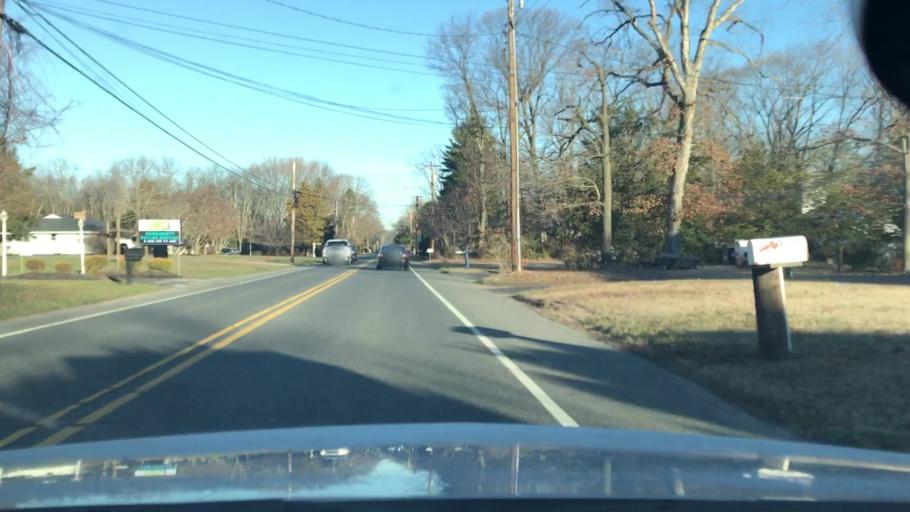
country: US
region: New Jersey
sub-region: Gloucester County
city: Williamstown
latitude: 39.7066
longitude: -75.0213
